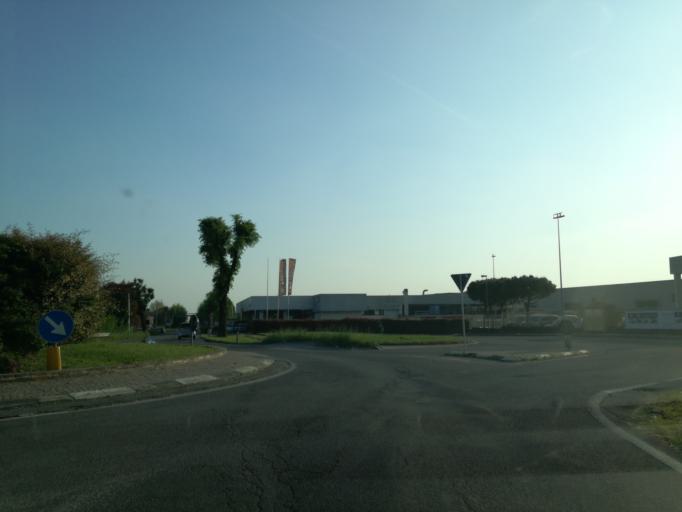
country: IT
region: Lombardy
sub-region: Provincia di Lecco
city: Merate
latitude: 45.6788
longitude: 9.4283
